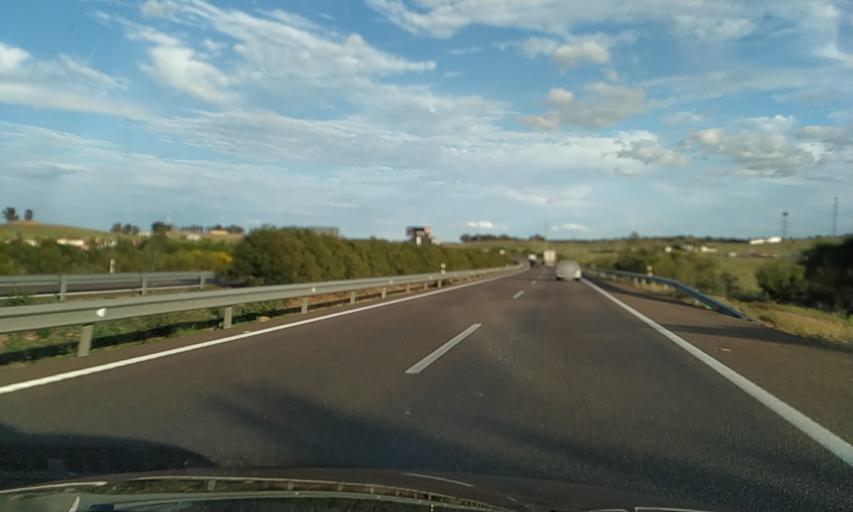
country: ES
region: Extremadura
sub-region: Provincia de Badajoz
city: Badajoz
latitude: 38.8809
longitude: -6.8878
